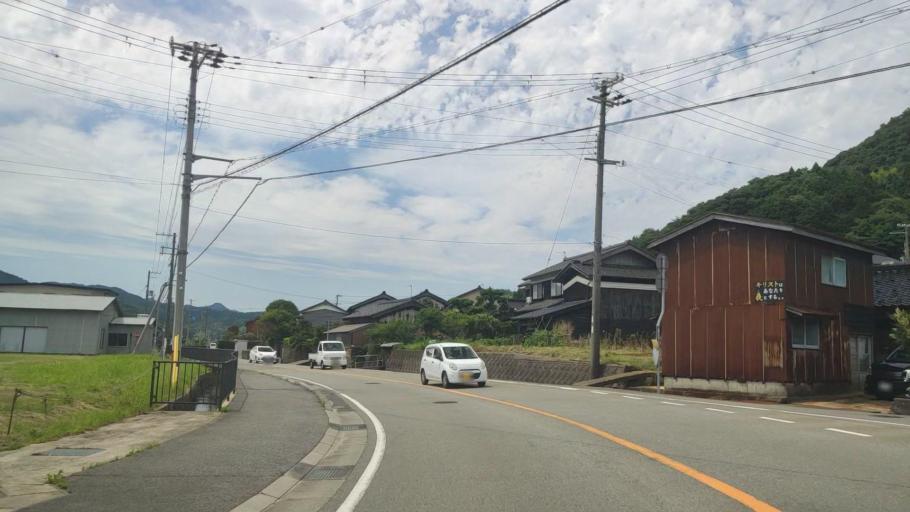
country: JP
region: Hyogo
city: Toyooka
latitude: 35.6462
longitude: 134.7580
